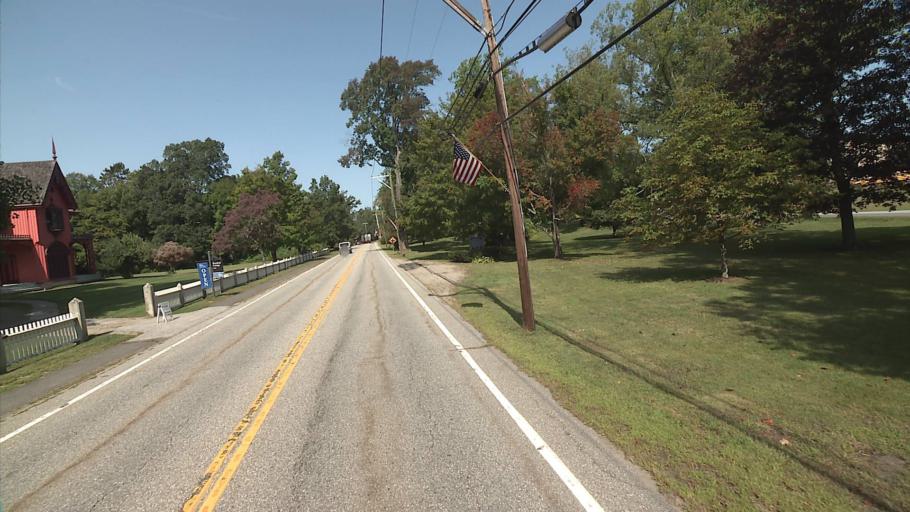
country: US
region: Connecticut
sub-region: Windham County
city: South Woodstock
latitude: 41.9494
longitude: -71.9755
